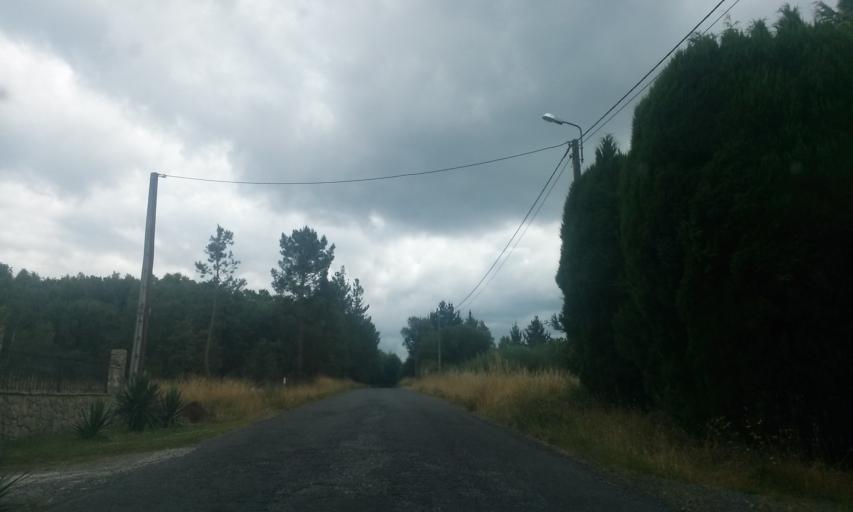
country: ES
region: Galicia
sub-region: Provincia de Lugo
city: Outeiro de Rei
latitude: 43.0750
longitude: -7.6292
